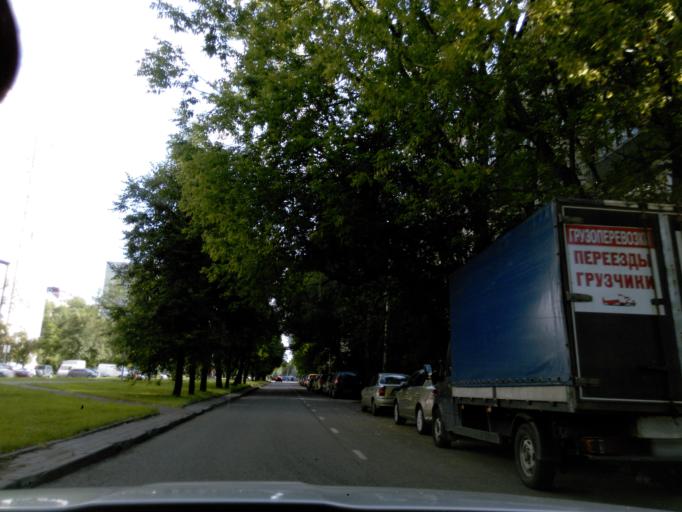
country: RU
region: Moskovskaya
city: Koptevo
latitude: 55.8336
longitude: 37.5284
